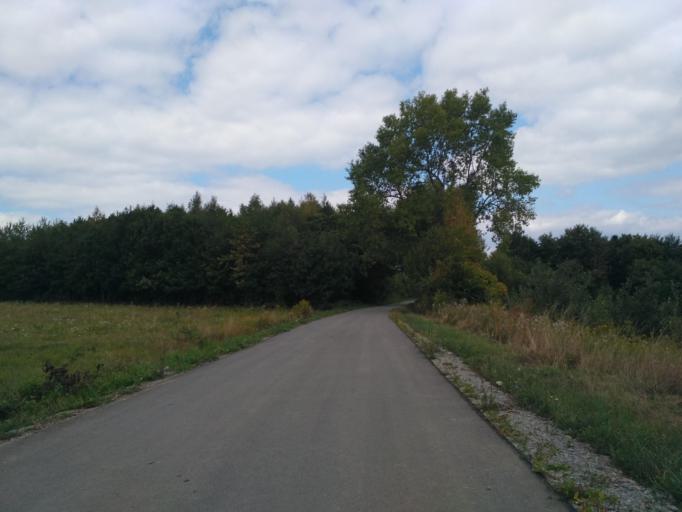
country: PL
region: Subcarpathian Voivodeship
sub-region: Powiat rzeszowski
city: Dynow
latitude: 49.7759
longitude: 22.2792
